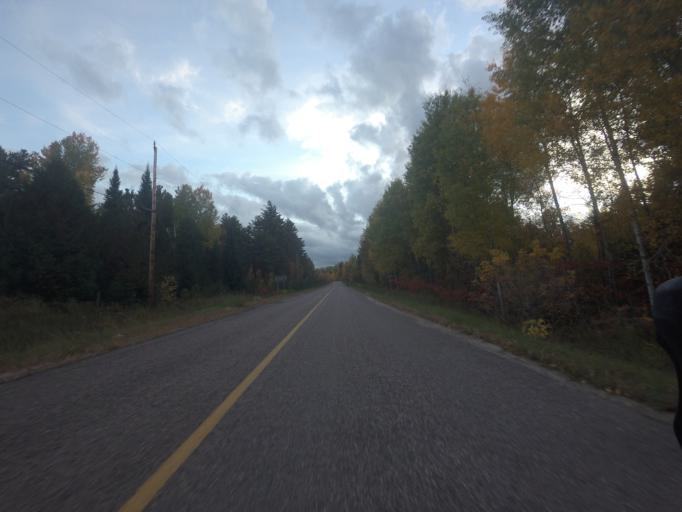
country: CA
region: Ontario
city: Renfrew
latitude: 45.3883
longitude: -76.9527
